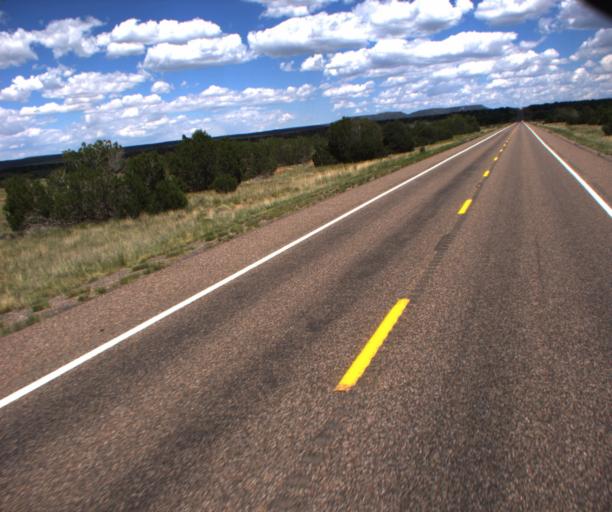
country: US
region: Arizona
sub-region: Apache County
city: Springerville
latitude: 34.1524
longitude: -109.1553
